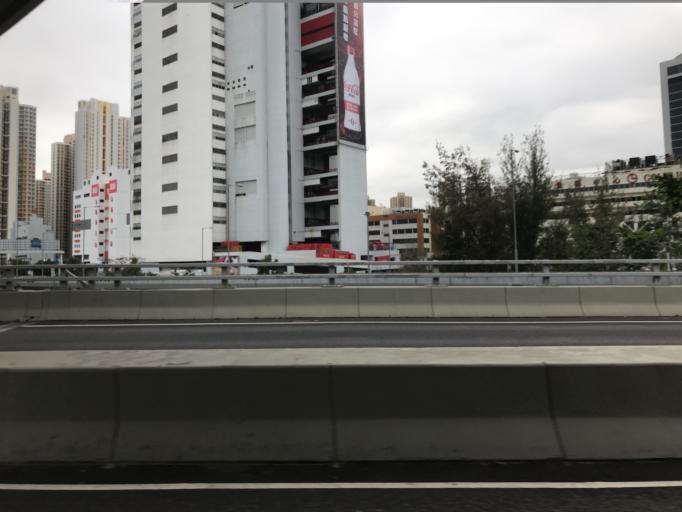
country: HK
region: Sha Tin
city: Sha Tin
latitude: 22.3823
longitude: 114.2103
